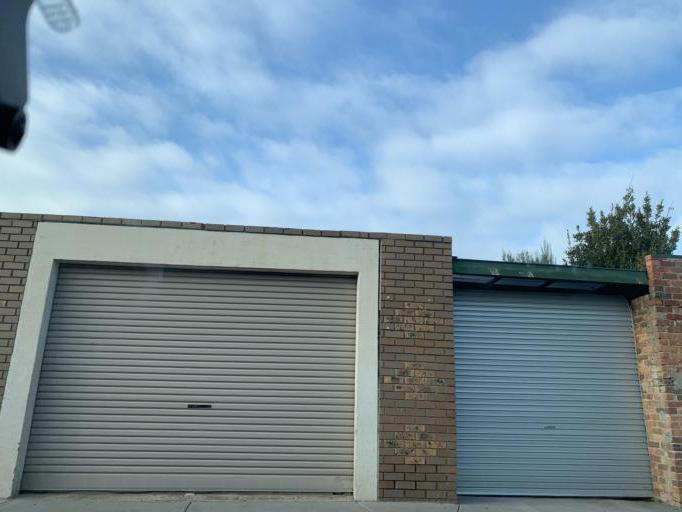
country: AU
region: Victoria
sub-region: Moreland
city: Coburg
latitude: -37.7460
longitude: 144.9678
